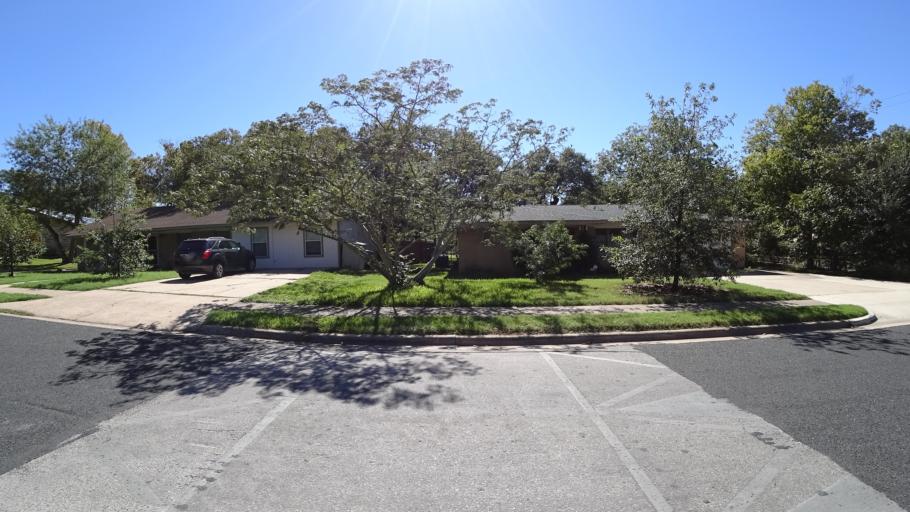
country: US
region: Texas
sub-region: Travis County
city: Rollingwood
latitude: 30.2279
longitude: -97.7958
